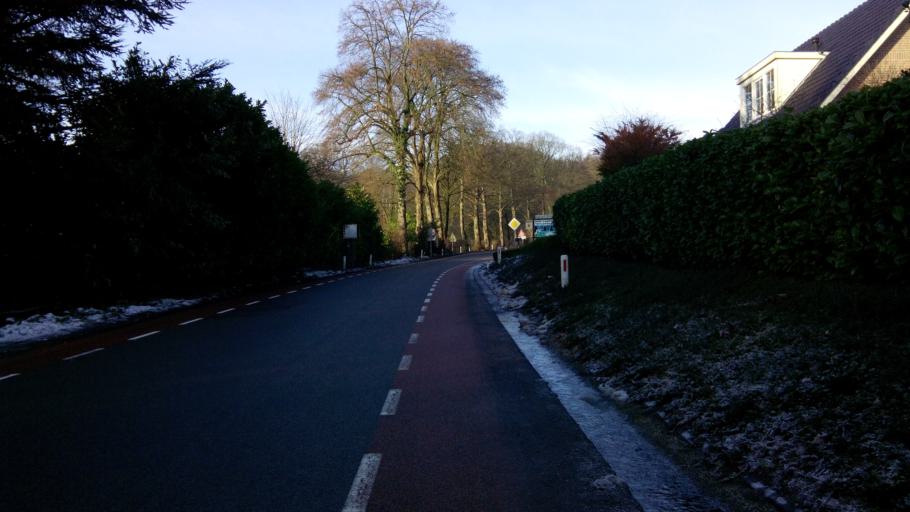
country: NL
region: Gelderland
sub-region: Gemeente Groesbeek
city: Berg en Dal
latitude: 51.8148
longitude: 5.9378
